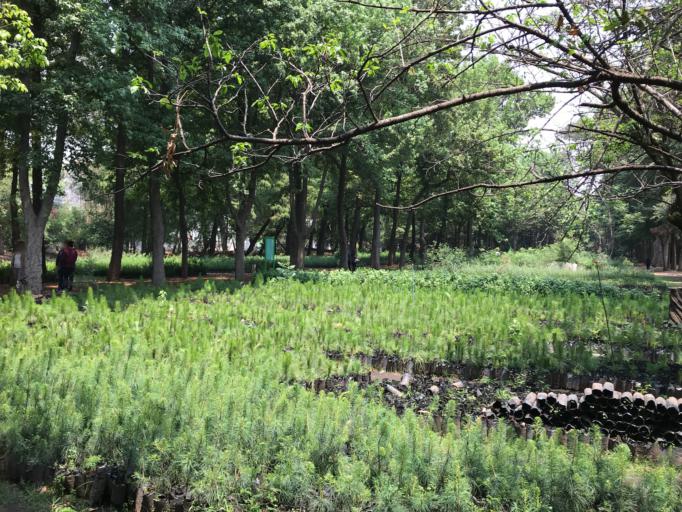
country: MX
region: Mexico City
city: Coyoacan
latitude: 19.3520
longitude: -99.1763
